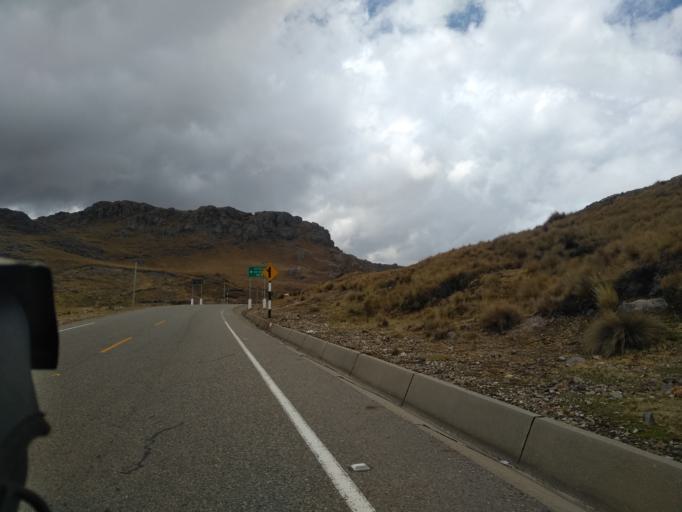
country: PE
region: La Libertad
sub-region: Provincia de Santiago de Chuco
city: Quiruvilca
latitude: -7.9737
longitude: -78.2093
